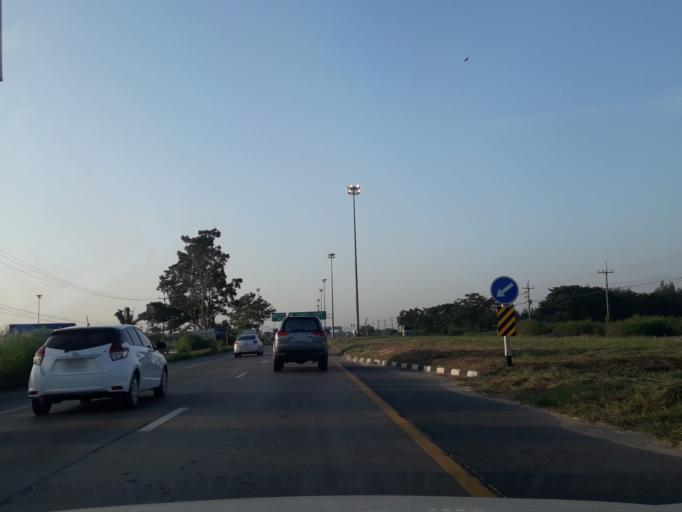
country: TH
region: Phra Nakhon Si Ayutthaya
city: Phra Nakhon Si Ayutthaya
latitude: 14.3097
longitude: 100.5265
